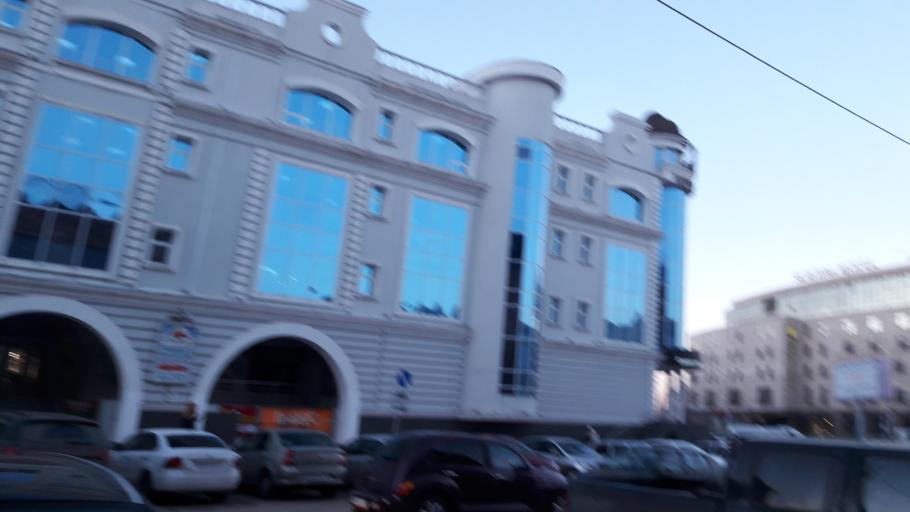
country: RU
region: Tula
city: Tula
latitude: 54.1925
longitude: 37.6130
